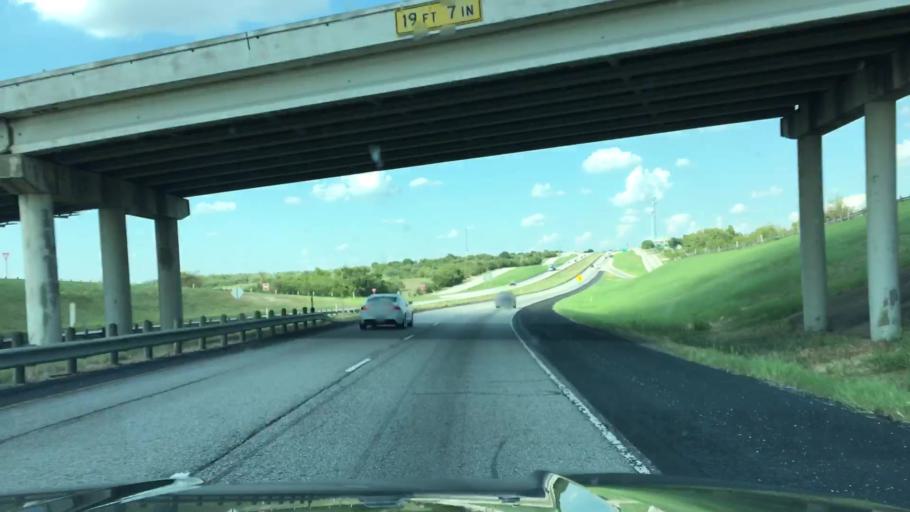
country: US
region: Texas
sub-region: Wise County
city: Rhome
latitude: 33.0554
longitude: -97.4788
